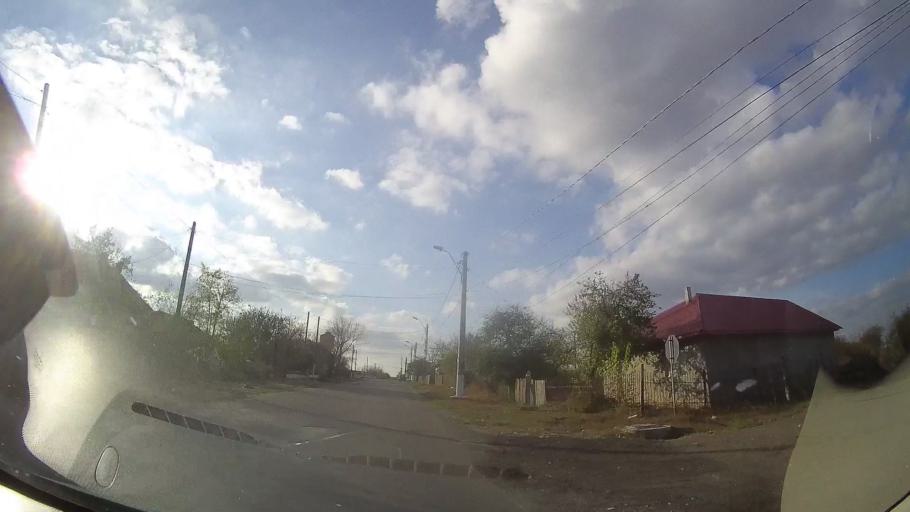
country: RO
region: Constanta
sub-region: Comuna Negru Voda
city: Negru Voda
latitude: 43.8194
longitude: 28.2264
